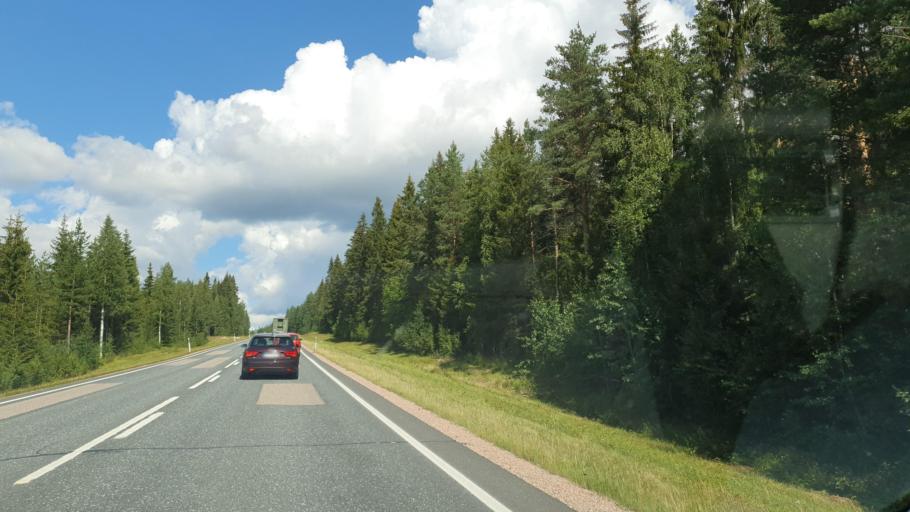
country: FI
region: Kainuu
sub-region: Kajaani
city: Kajaani
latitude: 64.0865
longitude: 27.4530
